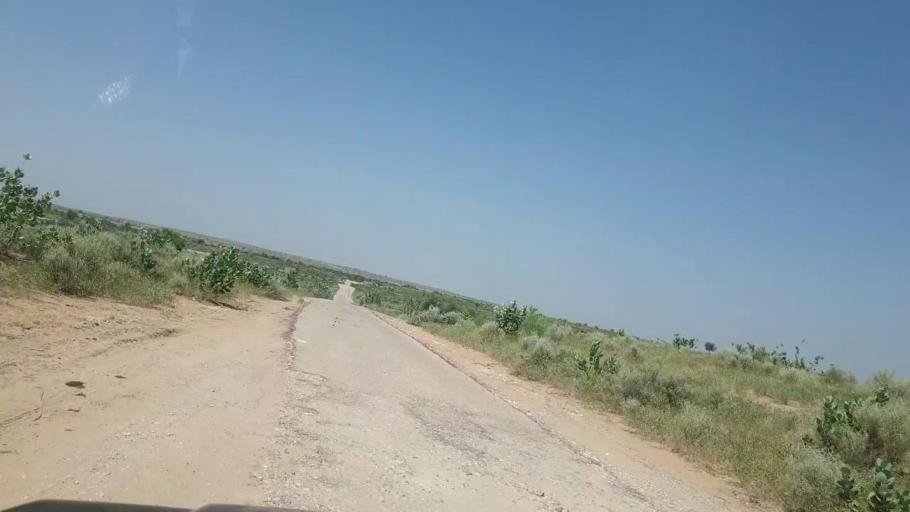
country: PK
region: Sindh
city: Chor
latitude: 25.3589
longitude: 70.3303
